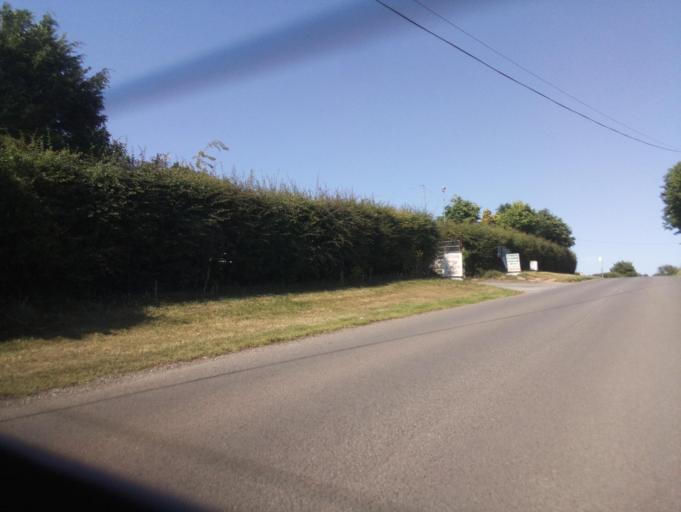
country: GB
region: England
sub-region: Devon
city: Marldon
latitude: 50.4097
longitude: -3.6154
